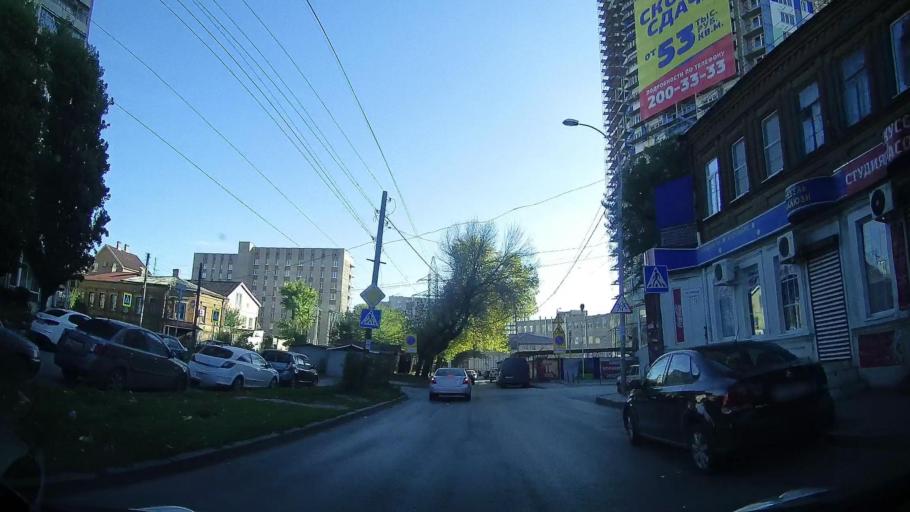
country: RU
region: Rostov
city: Rostov-na-Donu
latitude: 47.2265
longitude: 39.6915
